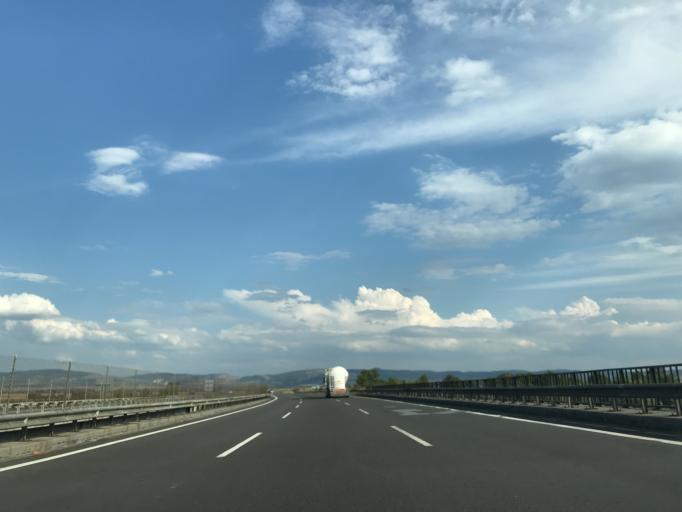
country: TR
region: Bolu
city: Gerede
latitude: 40.7258
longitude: 32.2076
